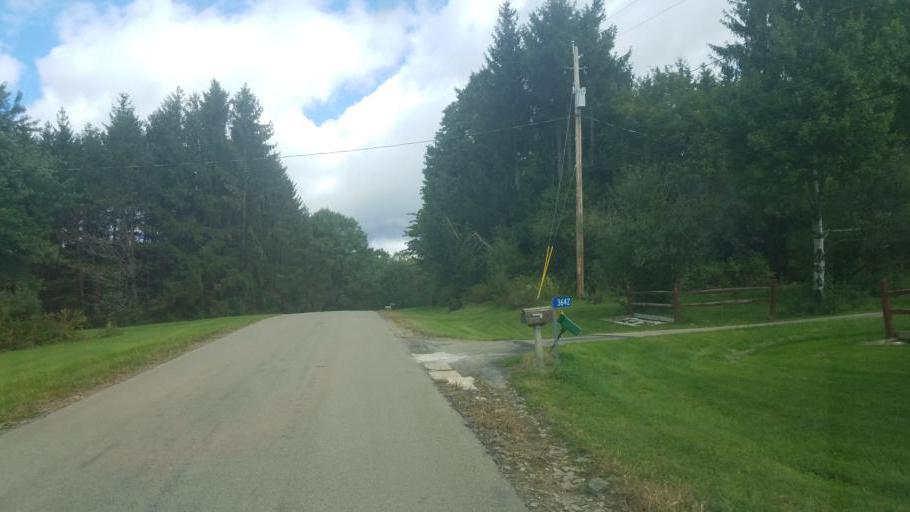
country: US
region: New York
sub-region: Cattaraugus County
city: Weston Mills
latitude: 42.1564
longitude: -78.3631
